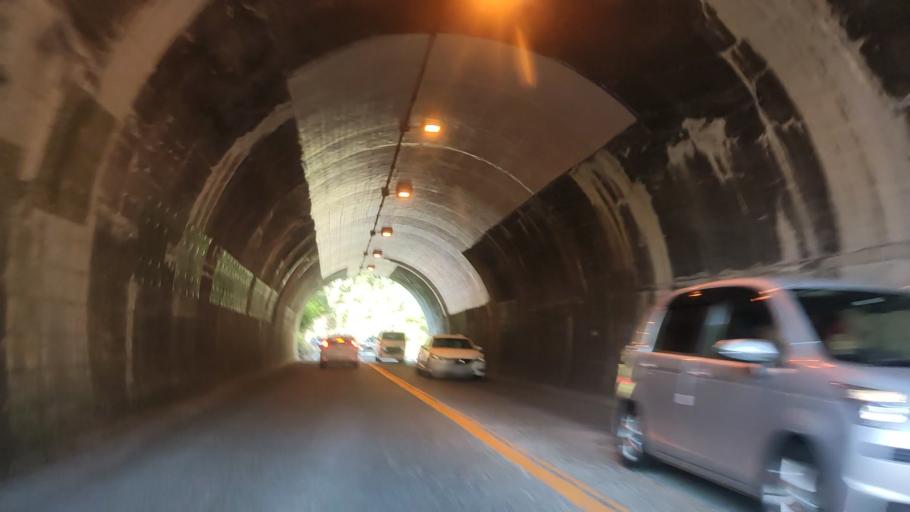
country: JP
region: Hyogo
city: Kobe
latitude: 34.6987
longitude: 135.1644
